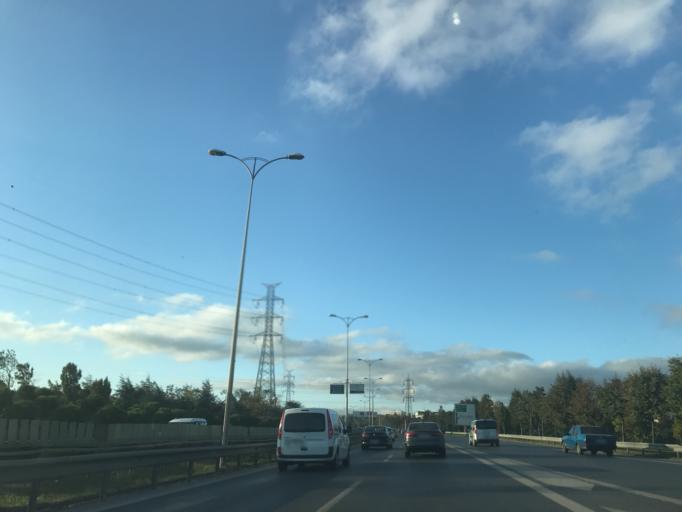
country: TR
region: Istanbul
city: Esenler
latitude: 41.0605
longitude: 28.8855
